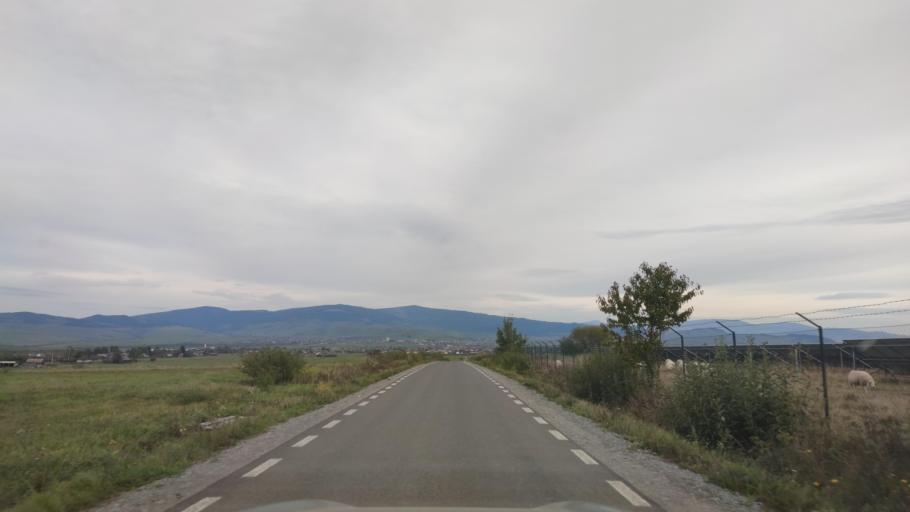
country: RO
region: Harghita
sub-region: Comuna Remetea
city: Remetea
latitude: 46.8067
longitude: 25.4194
